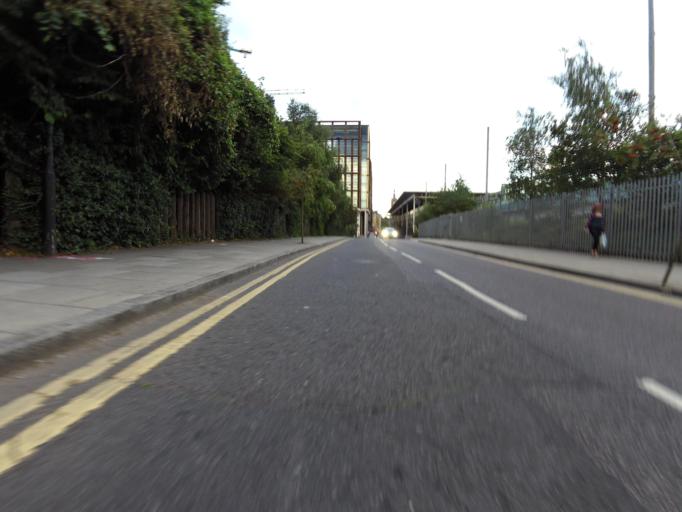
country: GB
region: England
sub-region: Greater London
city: Barnsbury
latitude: 51.5352
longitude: -0.1280
